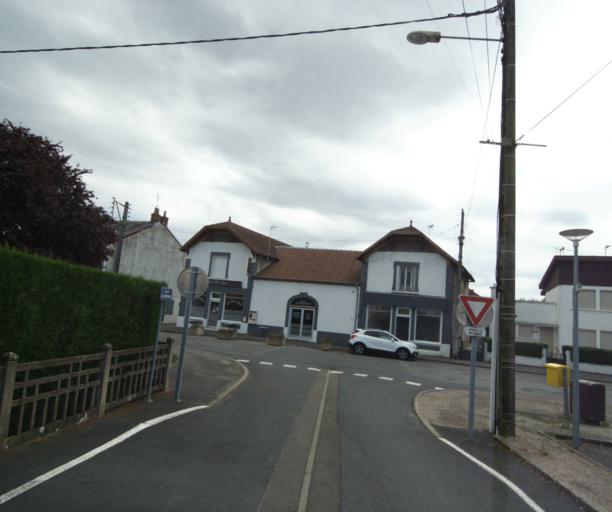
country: FR
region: Bourgogne
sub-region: Departement de Saone-et-Loire
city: Gueugnon
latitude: 46.6059
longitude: 4.0504
